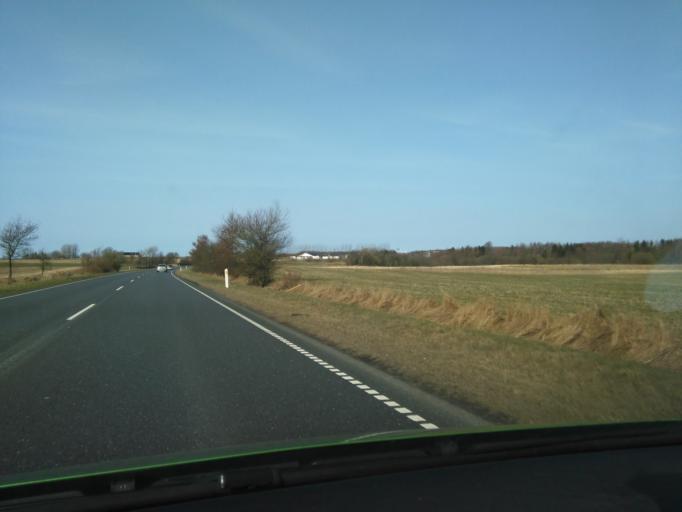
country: DK
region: Central Jutland
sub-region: Silkeborg Kommune
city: Kjellerup
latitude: 56.2693
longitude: 9.4224
